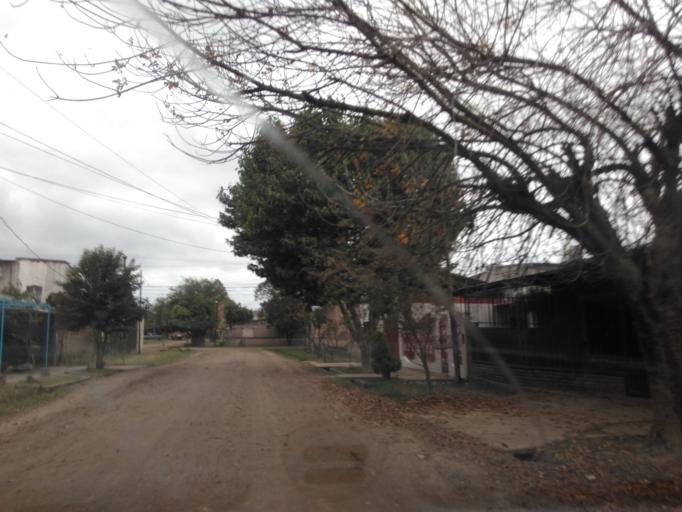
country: AR
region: Chaco
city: Fontana
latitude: -27.4316
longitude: -59.0166
